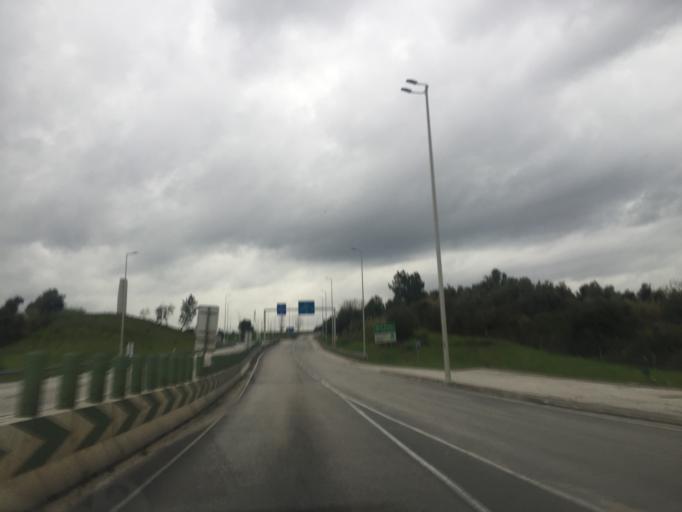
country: PT
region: Coimbra
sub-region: Condeixa-A-Nova
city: Condeixa-a-Nova
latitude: 40.1312
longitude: -8.4923
